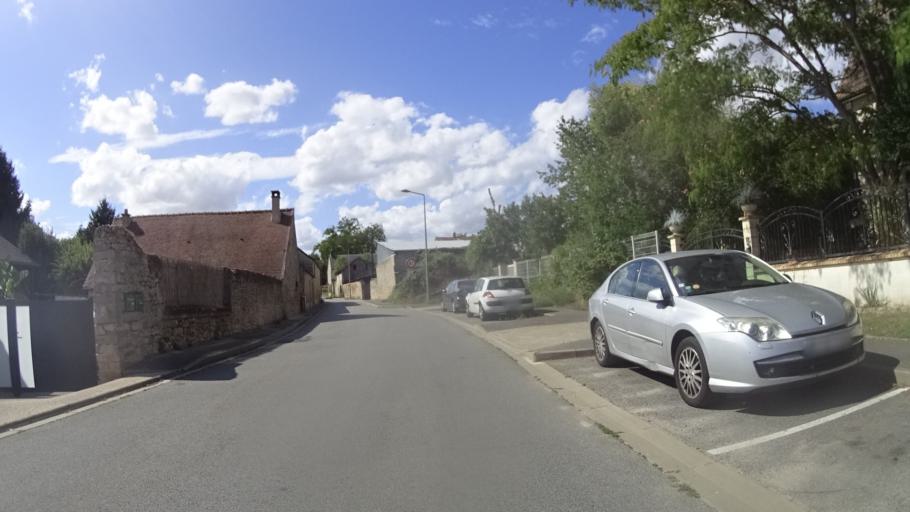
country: FR
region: Ile-de-France
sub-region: Departement de l'Essonne
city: Boutigny-sur-Essonne
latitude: 48.4544
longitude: 2.3615
